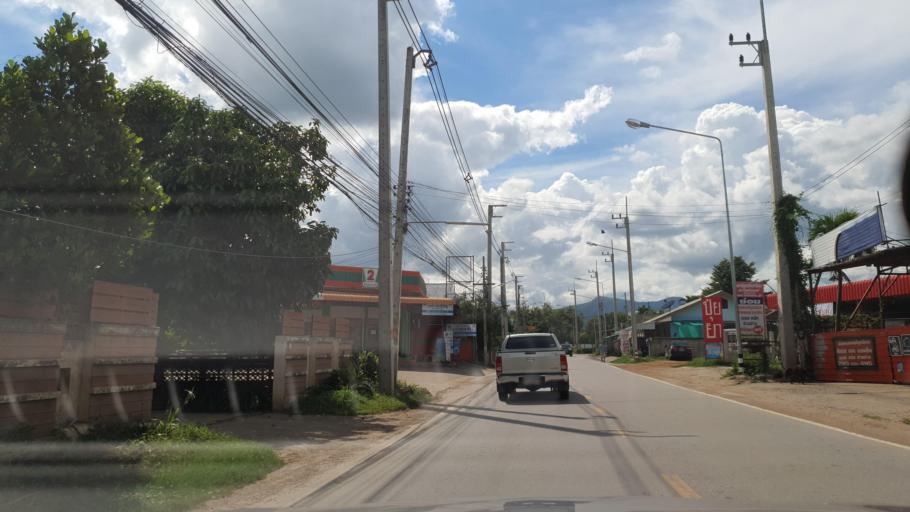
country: TH
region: Chiang Mai
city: Mae Wang
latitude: 18.6017
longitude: 98.8083
